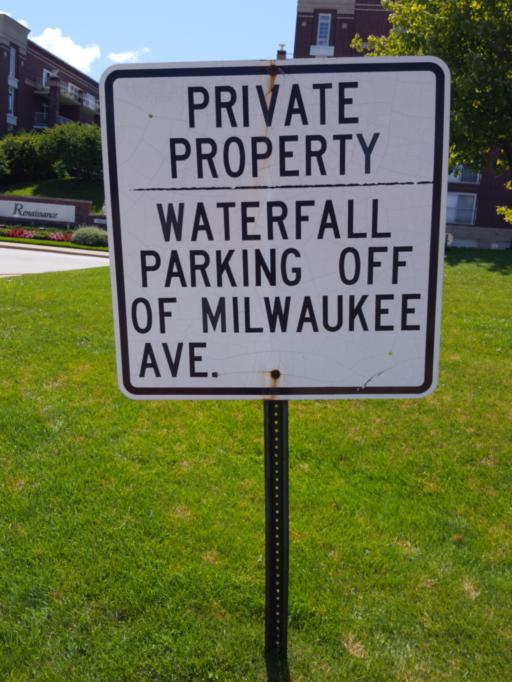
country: US
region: Illinois
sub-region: Cook County
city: Niles
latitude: 42.0116
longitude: -87.8034
